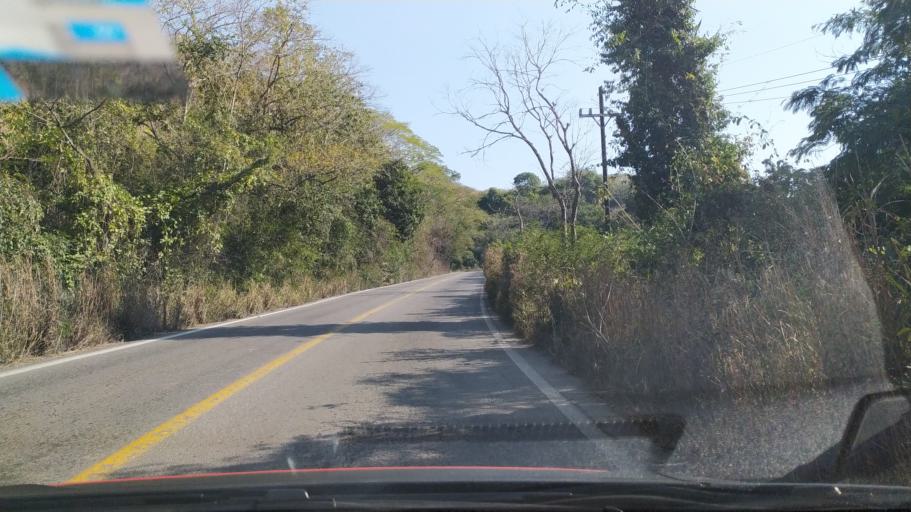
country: MX
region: Michoacan
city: Coahuayana Viejo
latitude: 18.6125
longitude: -103.6780
